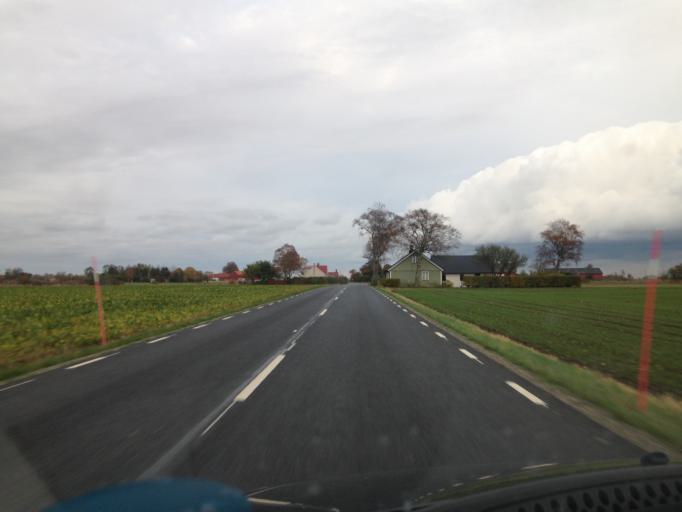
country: SE
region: Skane
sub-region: Simrishamns Kommun
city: Simrishamn
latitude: 55.4285
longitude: 14.1613
